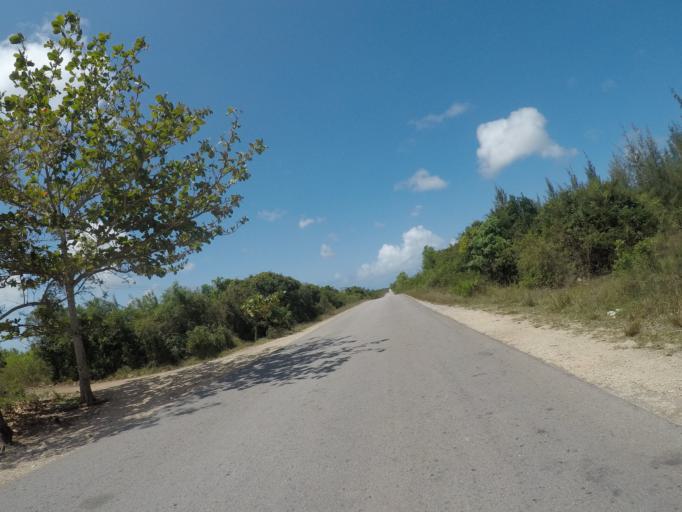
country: TZ
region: Zanzibar Central/South
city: Nganane
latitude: -6.2787
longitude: 39.4797
